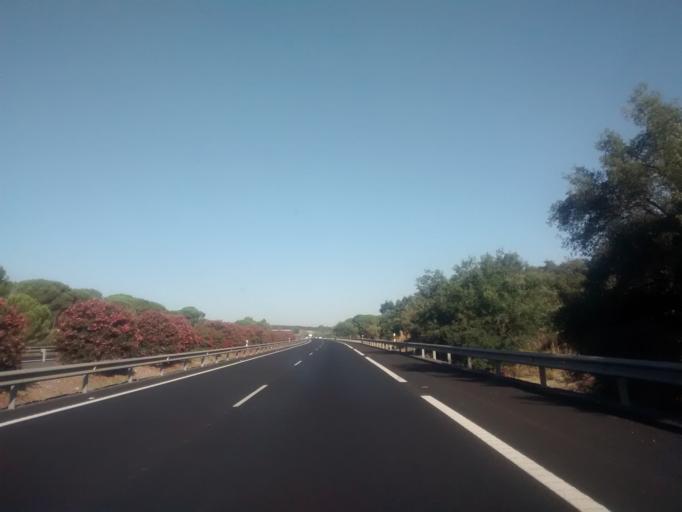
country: ES
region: Andalusia
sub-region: Provincia de Huelva
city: Villalba del Alcor
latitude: 37.3477
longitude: -6.4623
